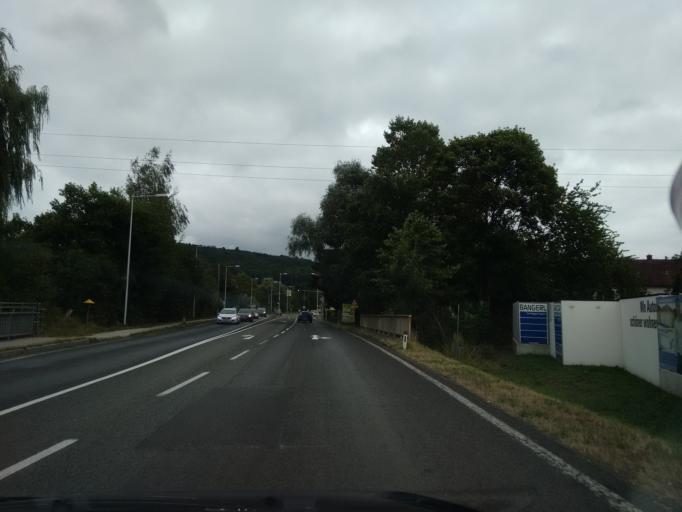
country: AT
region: Upper Austria
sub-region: Politischer Bezirk Grieskirchen
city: Grieskirchen
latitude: 48.2199
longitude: 13.8699
